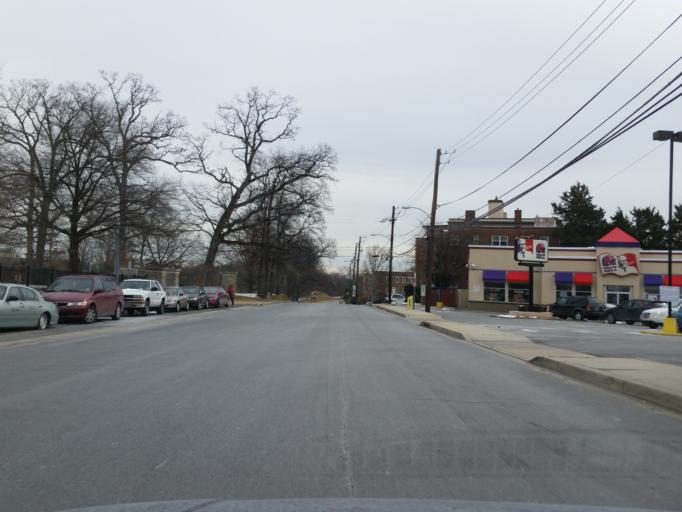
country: US
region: Maryland
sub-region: Montgomery County
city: Silver Spring
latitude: 38.9844
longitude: -77.0260
